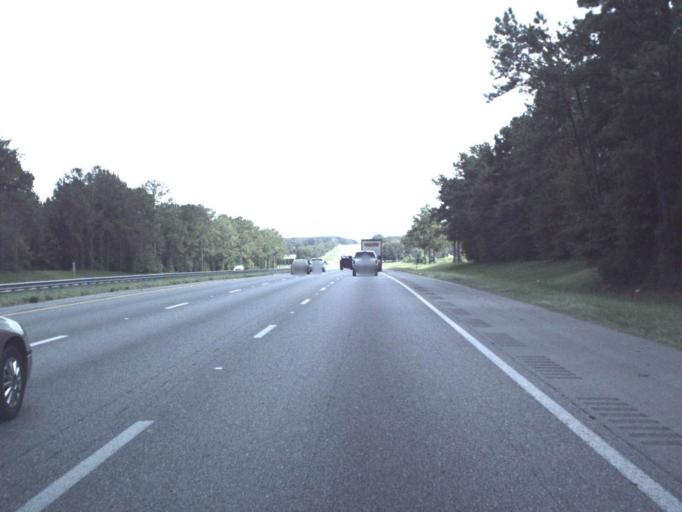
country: US
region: Florida
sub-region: Columbia County
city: Lake City
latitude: 30.0699
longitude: -82.6294
